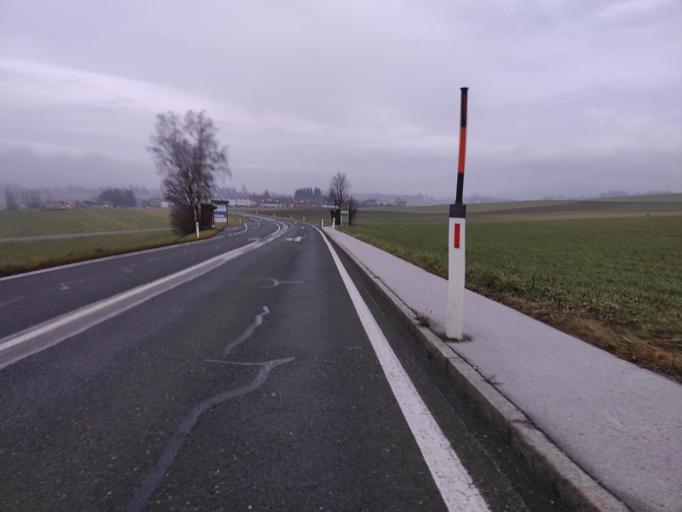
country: AT
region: Salzburg
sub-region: Politischer Bezirk Salzburg-Umgebung
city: Neumarkt am Wallersee
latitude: 47.9266
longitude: 13.2206
